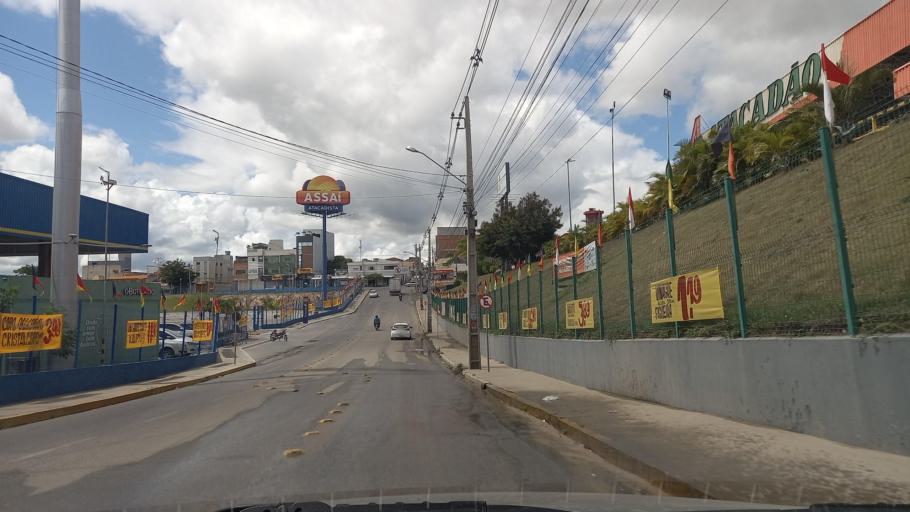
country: BR
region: Pernambuco
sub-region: Caruaru
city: Caruaru
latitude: -8.2961
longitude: -35.9720
